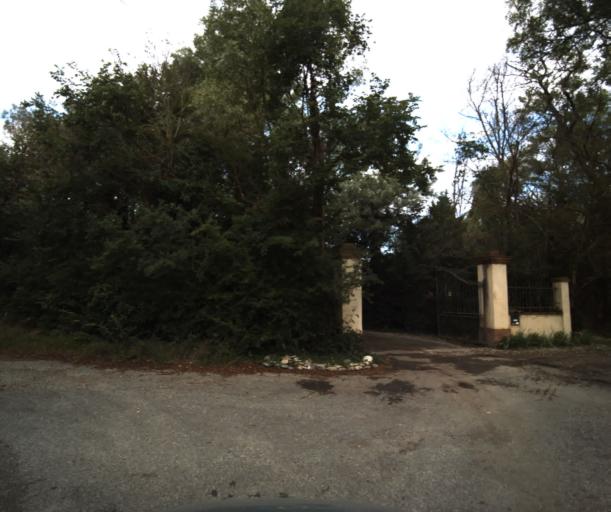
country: FR
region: Midi-Pyrenees
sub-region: Departement de la Haute-Garonne
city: Lherm
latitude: 43.4012
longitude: 1.2341
